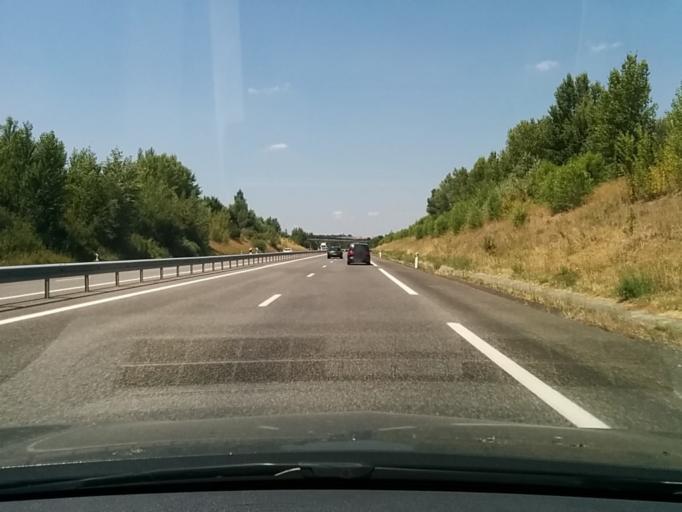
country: FR
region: Midi-Pyrenees
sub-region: Departement du Gers
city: Pujaudran
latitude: 43.6031
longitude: 1.0821
